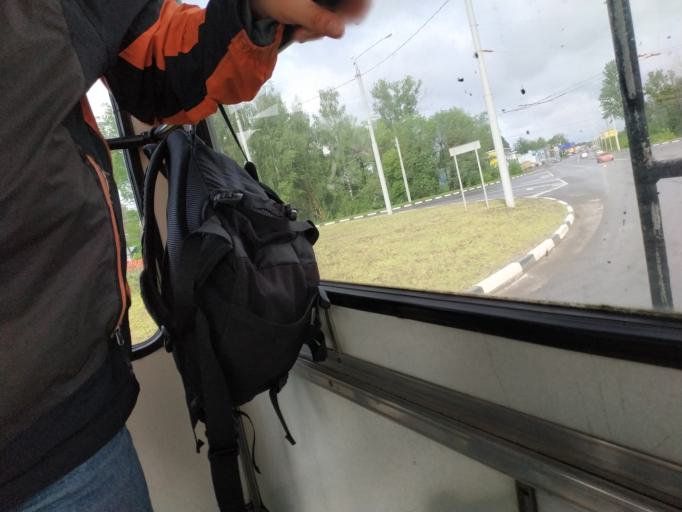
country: RU
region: Brjansk
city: Putevka
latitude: 53.2879
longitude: 34.3038
